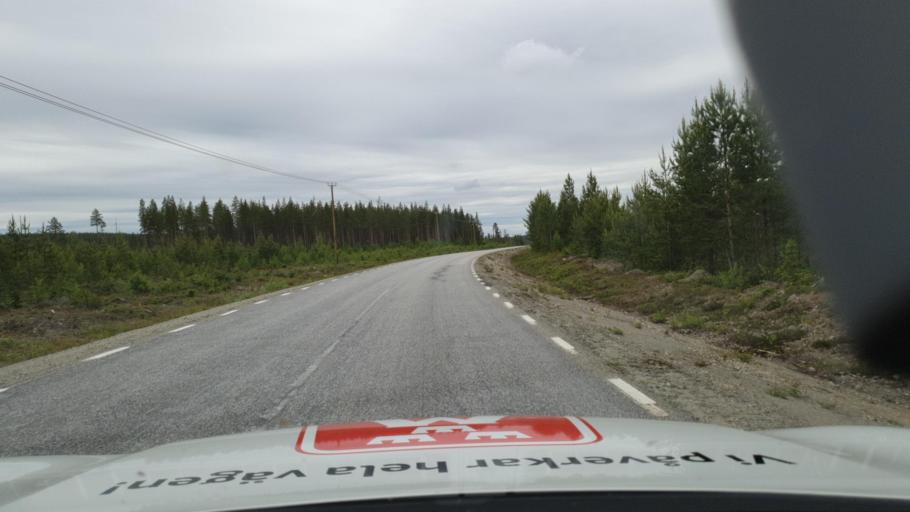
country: SE
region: Vaesterbotten
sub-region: Lycksele Kommun
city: Lycksele
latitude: 64.1155
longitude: 18.3635
